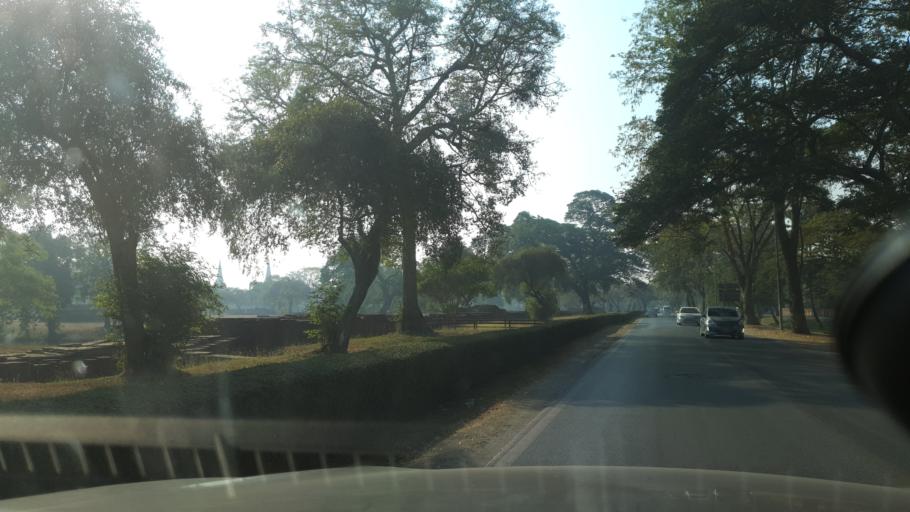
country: TH
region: Phra Nakhon Si Ayutthaya
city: Phra Nakhon Si Ayutthaya
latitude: 14.3596
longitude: 100.5554
